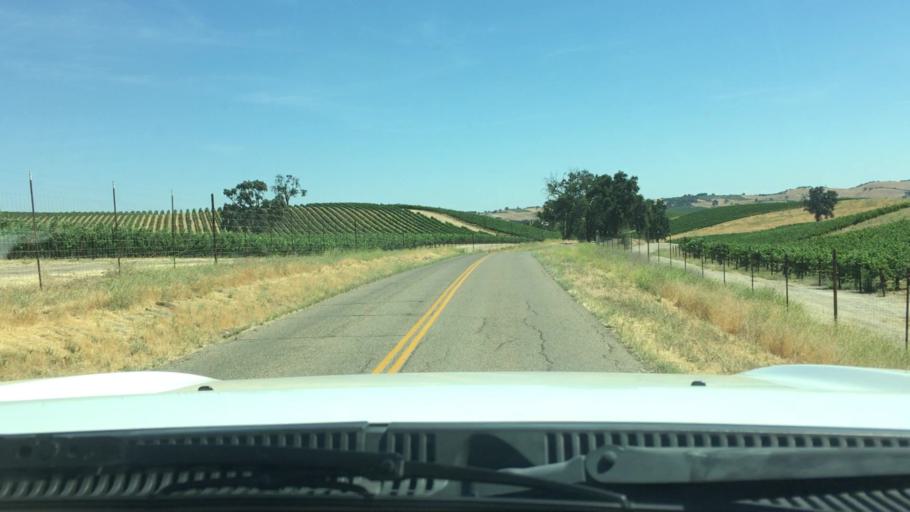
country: US
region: California
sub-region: San Luis Obispo County
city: Atascadero
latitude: 35.5592
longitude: -120.6101
